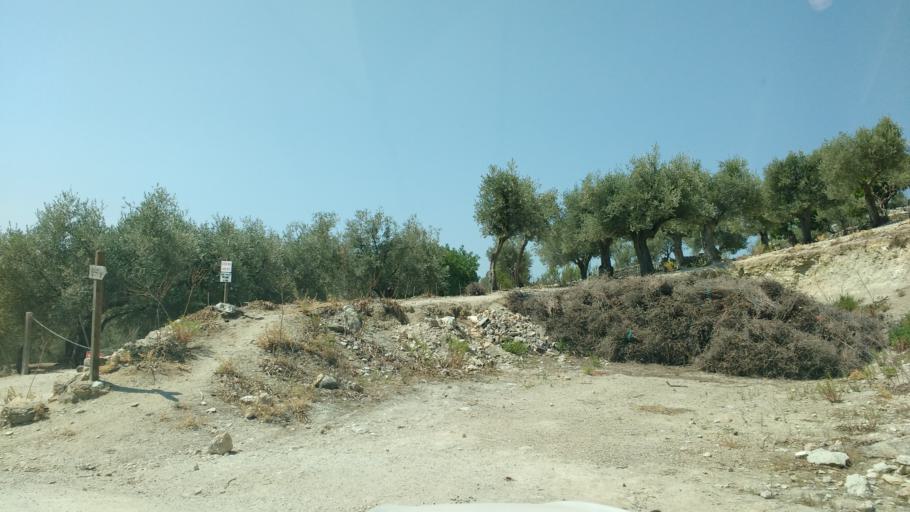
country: ES
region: Balearic Islands
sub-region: Illes Balears
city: Alaro
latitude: 39.7286
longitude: 2.7871
